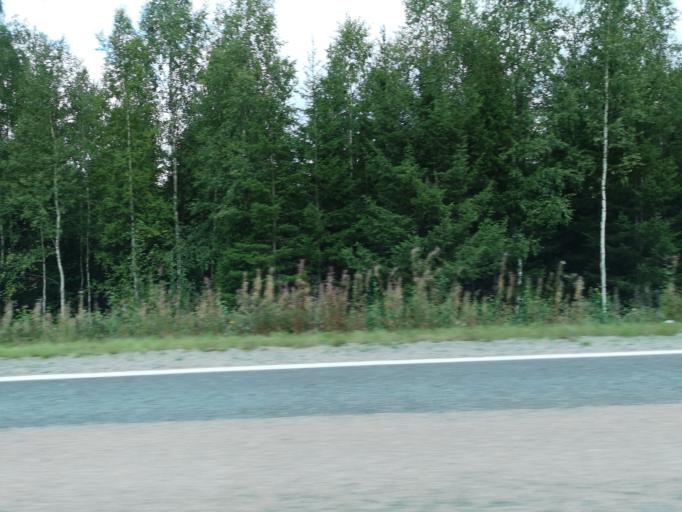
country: FI
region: Central Finland
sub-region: Jyvaeskylae
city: Hankasalmi
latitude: 62.3580
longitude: 26.5630
